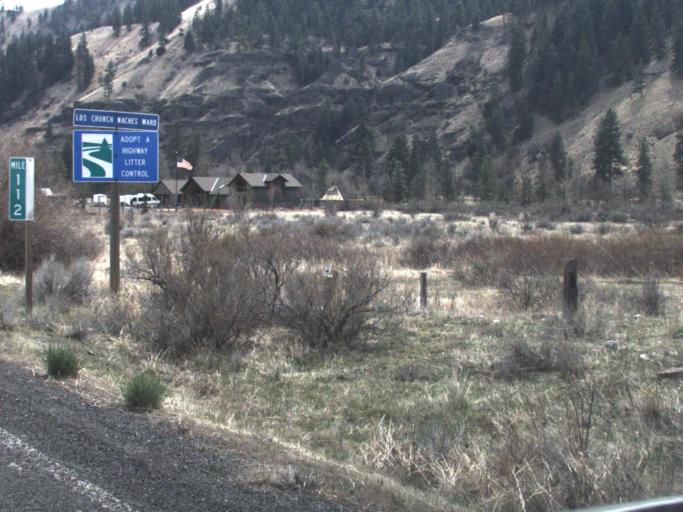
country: US
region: Washington
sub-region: Yakima County
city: Tieton
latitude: 46.7780
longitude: -120.8599
